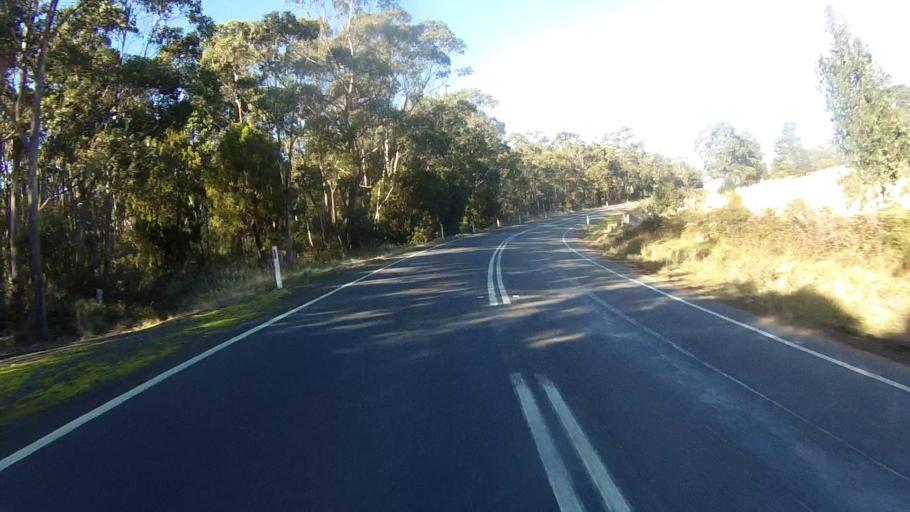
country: AU
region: Tasmania
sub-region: Sorell
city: Sorell
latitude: -42.8236
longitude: 147.8050
